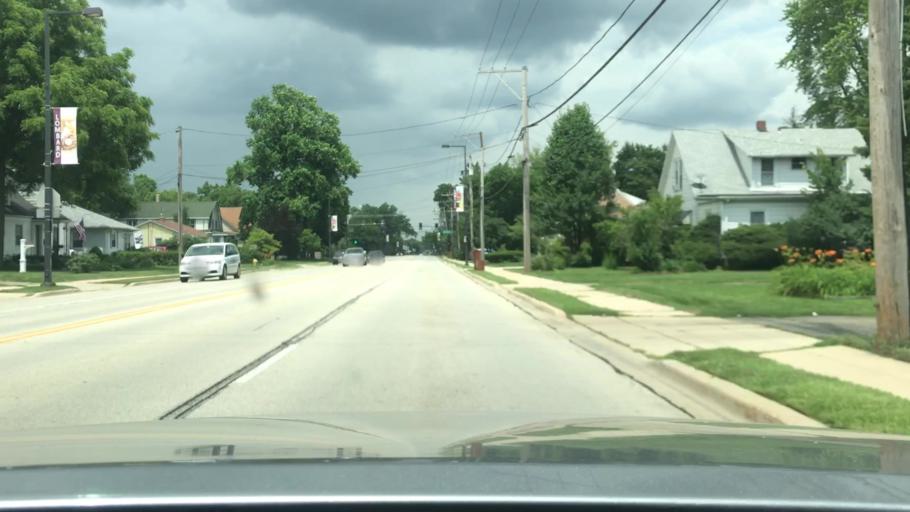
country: US
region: Illinois
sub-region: DuPage County
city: Villa Park
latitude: 41.8769
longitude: -87.9935
